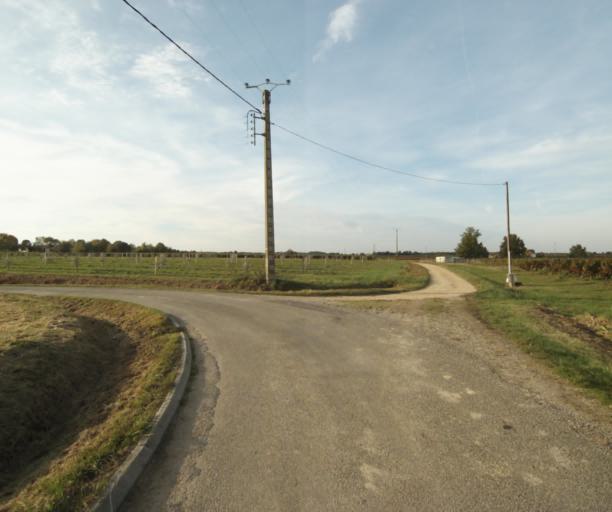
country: FR
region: Midi-Pyrenees
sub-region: Departement du Tarn-et-Garonne
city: Campsas
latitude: 43.8813
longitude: 1.3469
